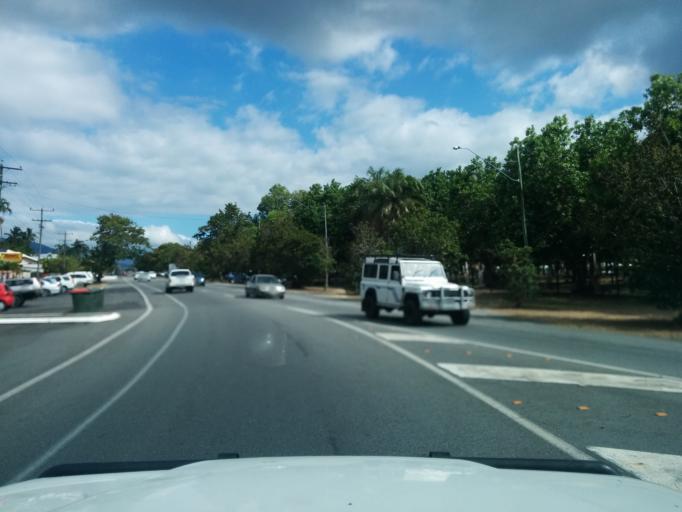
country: AU
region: Queensland
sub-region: Cairns
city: Cairns
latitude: -16.9145
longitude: 145.7643
